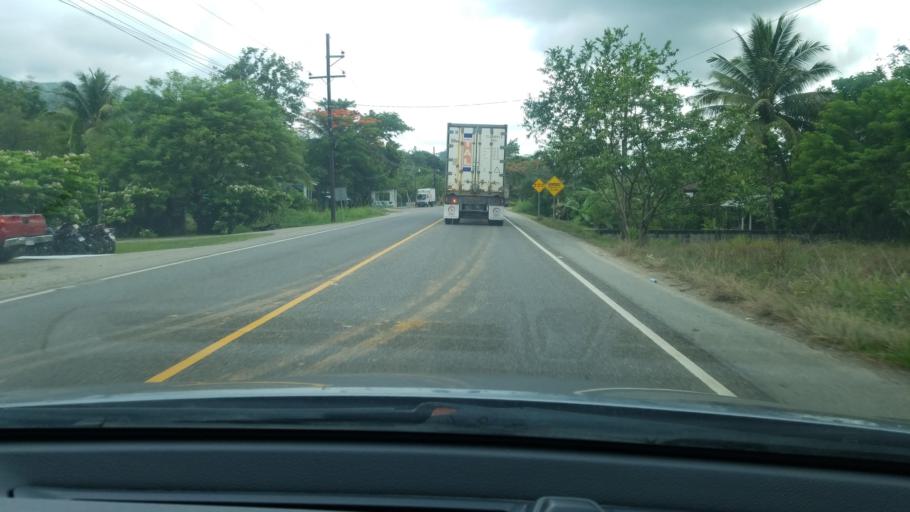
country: HN
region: Cortes
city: Potrerillos
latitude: 15.5926
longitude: -88.3241
